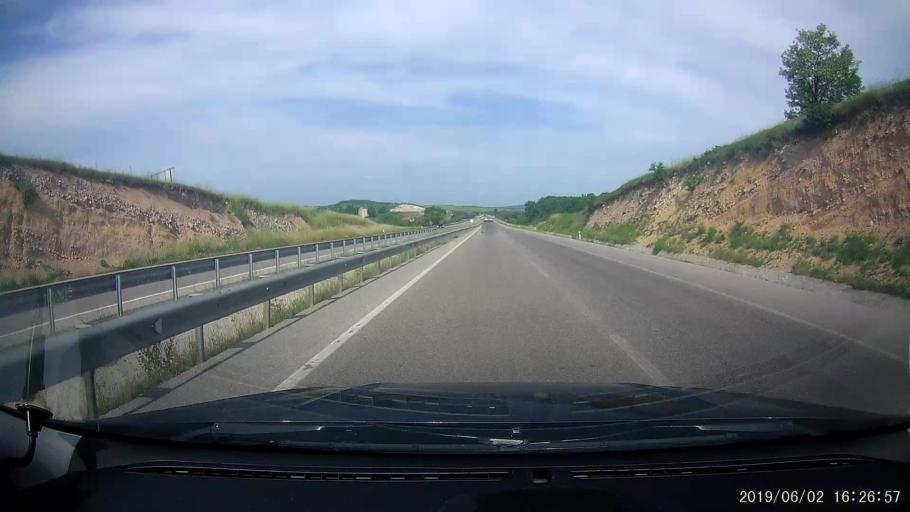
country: TR
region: Samsun
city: Ladik
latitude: 41.0017
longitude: 35.8162
